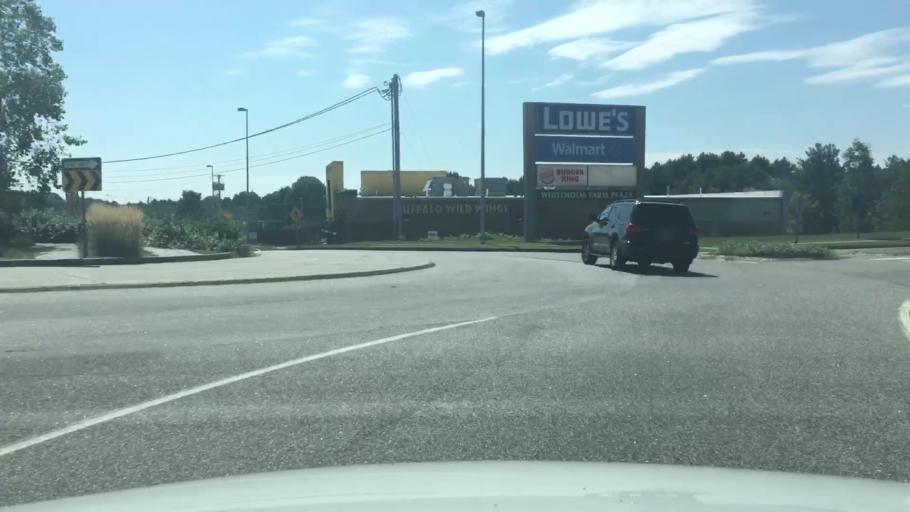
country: US
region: Maine
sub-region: Androscoggin County
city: Auburn
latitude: 44.1192
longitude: -70.2329
